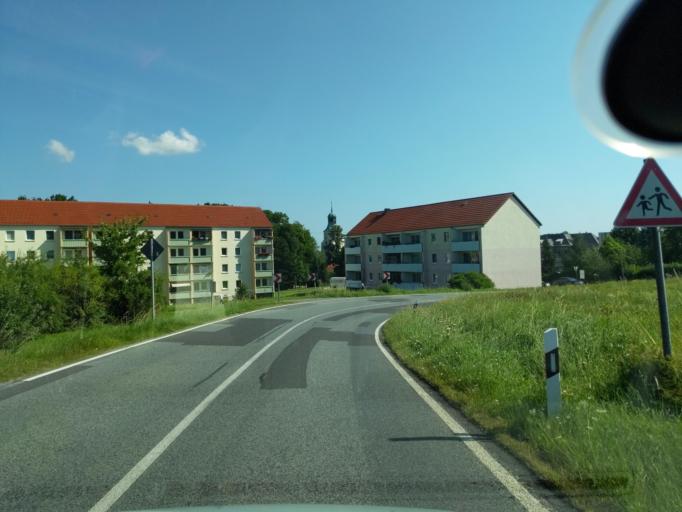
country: DE
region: Saxony
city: Lobau
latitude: 51.1298
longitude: 14.6730
